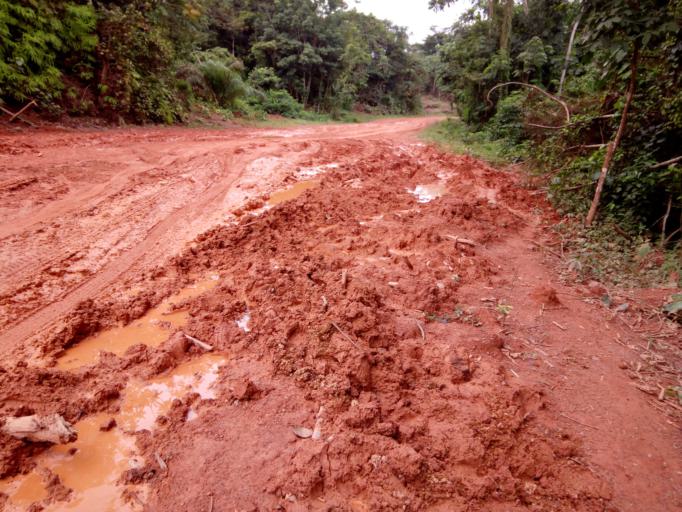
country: CI
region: Dix-Huit Montagnes
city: Toulepleu Guere
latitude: 6.4854
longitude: -8.7945
